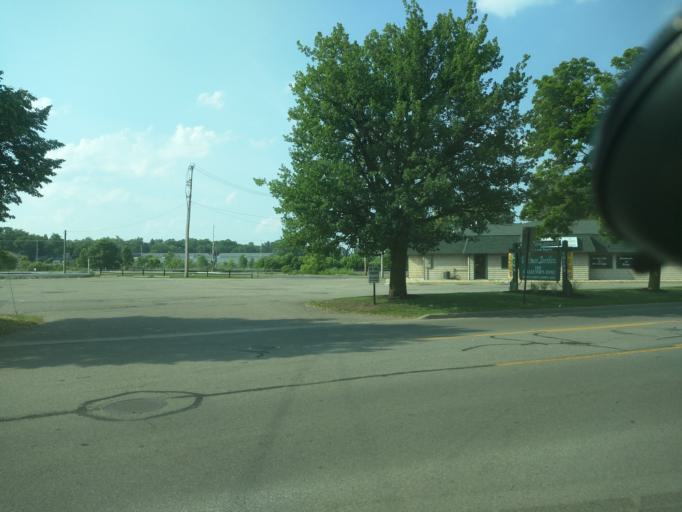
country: US
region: Michigan
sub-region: Jackson County
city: Jackson
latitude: 42.2520
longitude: -84.4320
